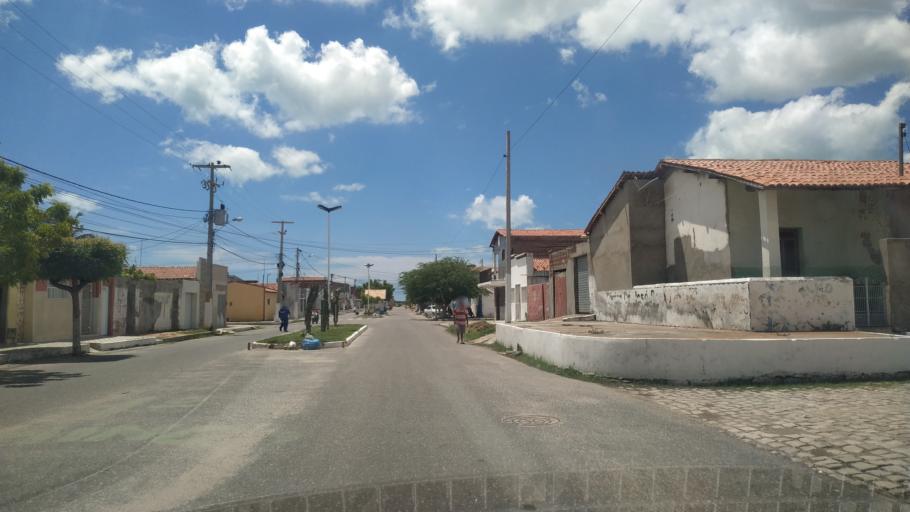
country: BR
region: Rio Grande do Norte
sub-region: Areia Branca
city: Areia Branca
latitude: -4.9530
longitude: -37.1303
